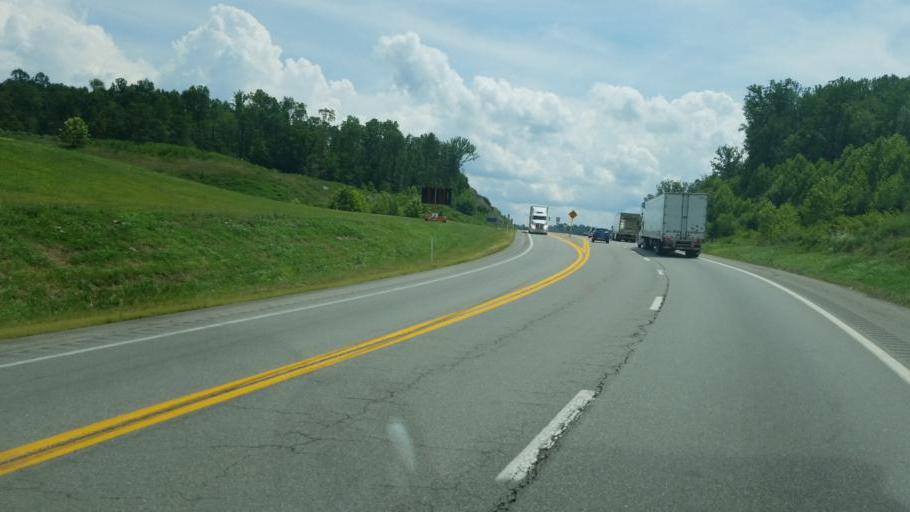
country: US
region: West Virginia
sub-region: Putnam County
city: Buffalo
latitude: 38.5779
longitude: -82.0165
